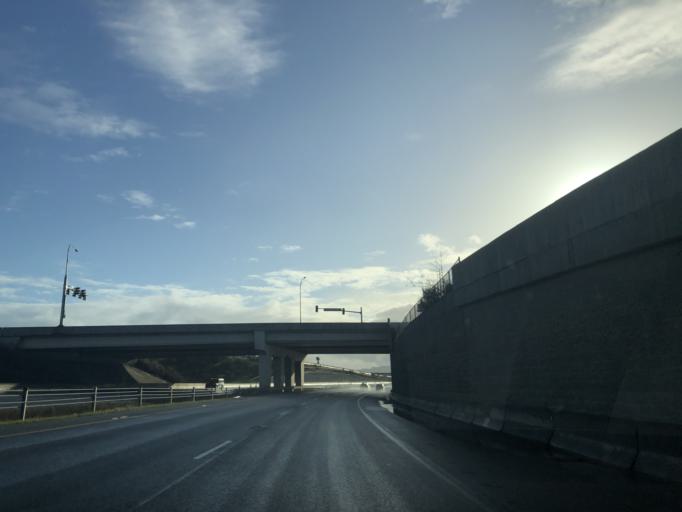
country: US
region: Washington
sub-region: Kitsap County
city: Silverdale
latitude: 47.6657
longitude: -122.6879
